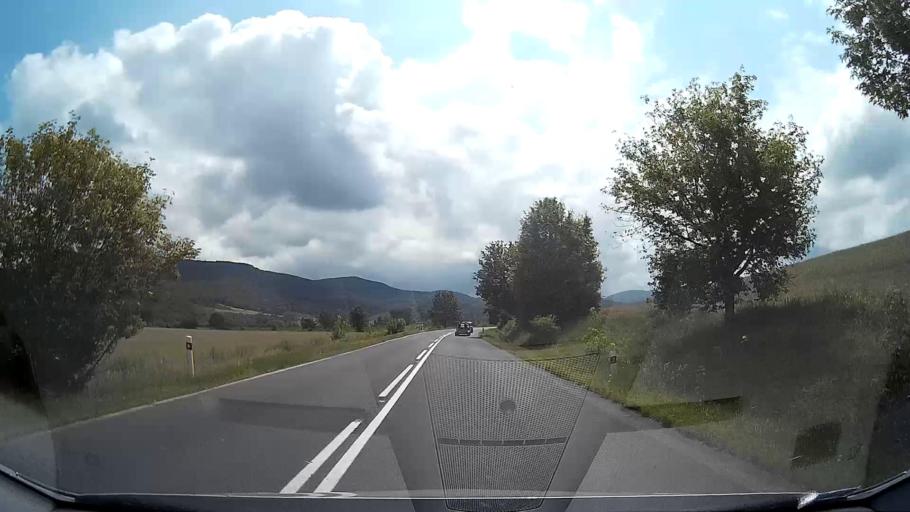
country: SK
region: Banskobystricky
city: Fil'akovo
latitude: 48.2432
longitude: 19.8370
